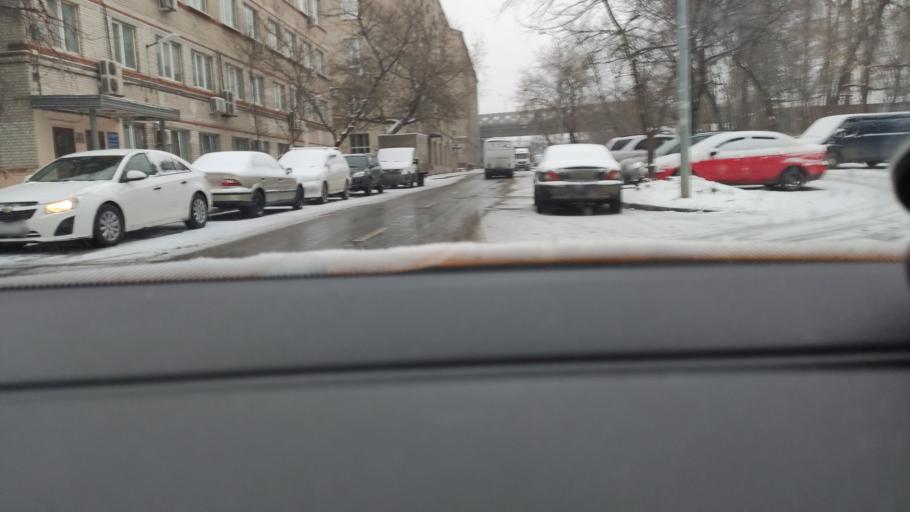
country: RU
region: Moscow
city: Zapadnoye Degunino
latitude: 55.8565
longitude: 37.5309
